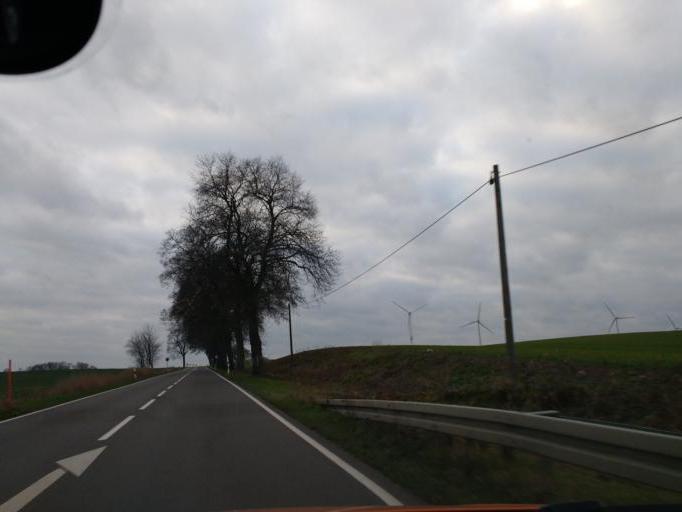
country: DE
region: Brandenburg
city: Wriezen
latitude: 52.6809
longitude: 14.0899
